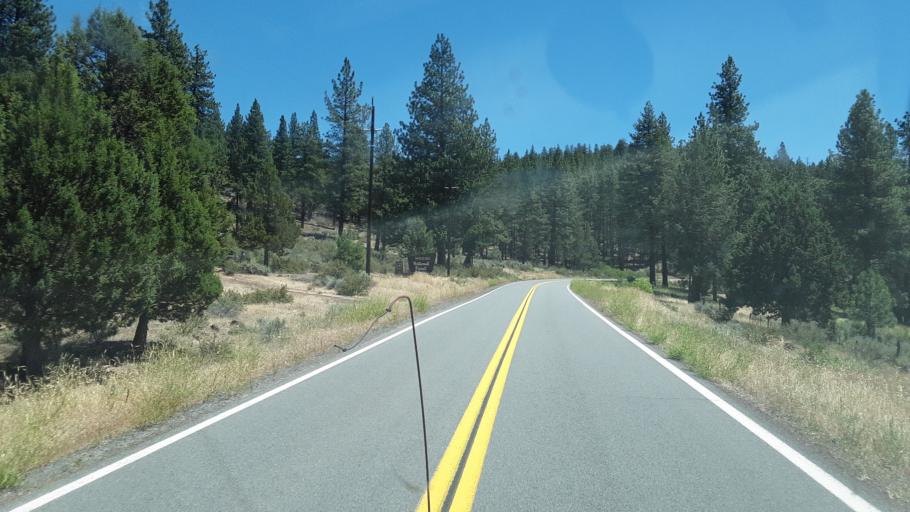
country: US
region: California
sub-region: Modoc County
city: Alturas
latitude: 41.0347
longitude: -120.8560
